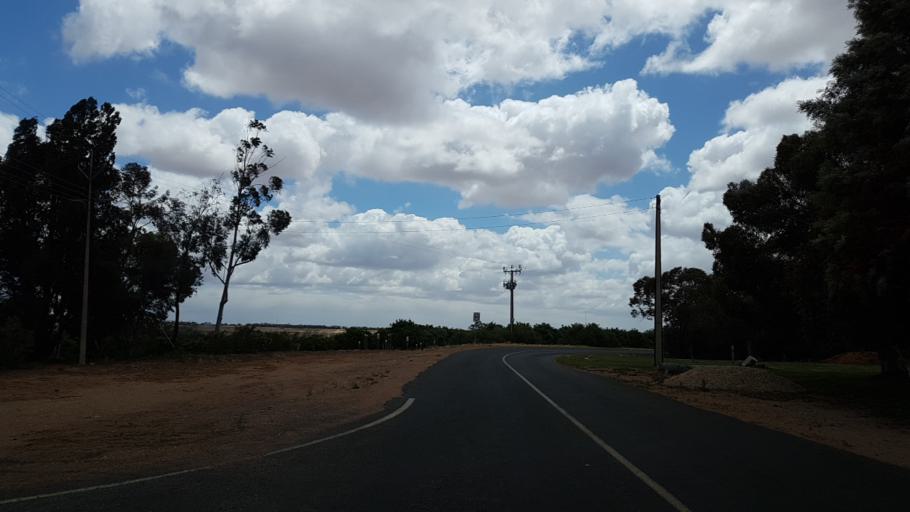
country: AU
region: South Australia
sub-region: Loxton Waikerie
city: Waikerie
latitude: -34.1707
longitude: 140.0323
